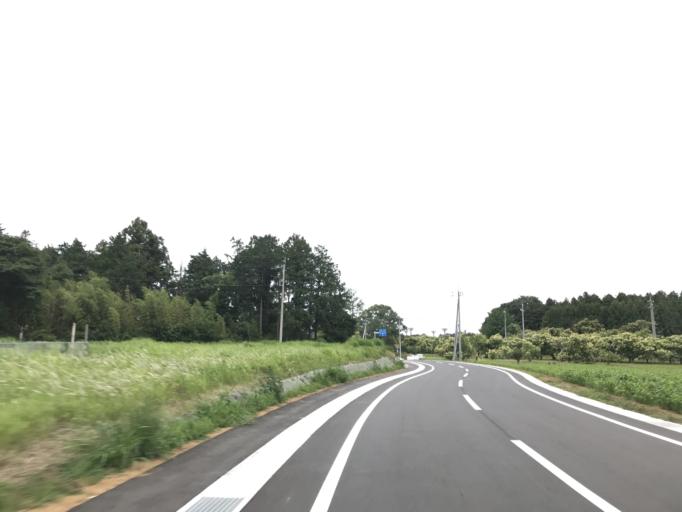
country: JP
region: Ibaraki
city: Ishioka
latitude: 36.2197
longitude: 140.2977
